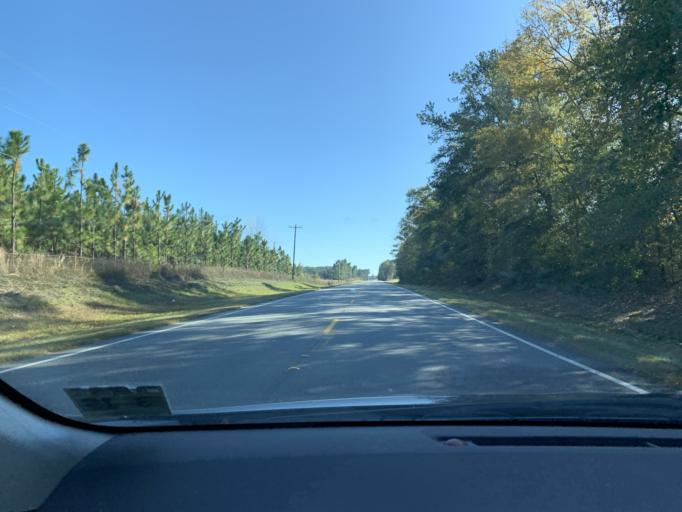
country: US
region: Georgia
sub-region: Coffee County
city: Broxton
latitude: 31.7698
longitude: -83.0301
